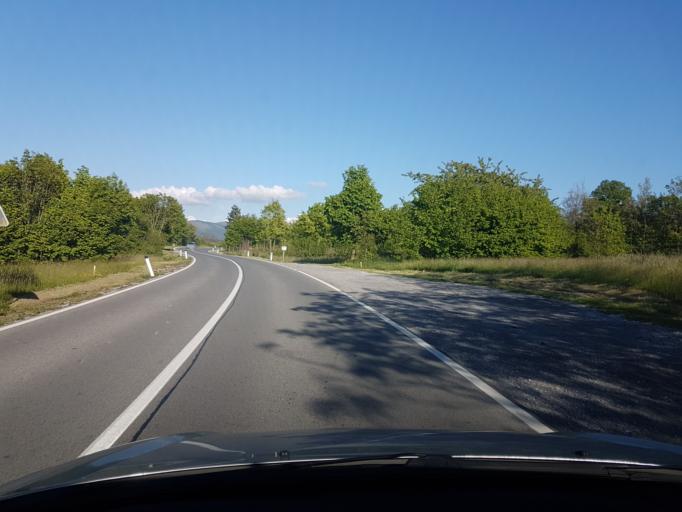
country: SI
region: Divaca
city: Divaca
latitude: 45.6989
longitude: 13.9384
